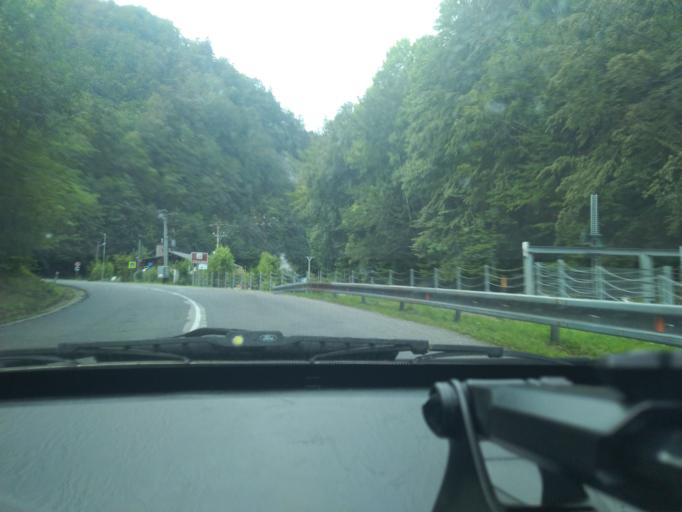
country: SK
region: Banskobystricky
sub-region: Okres Banska Bystrica
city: Banska Bystrica
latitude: 48.8183
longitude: 19.0403
